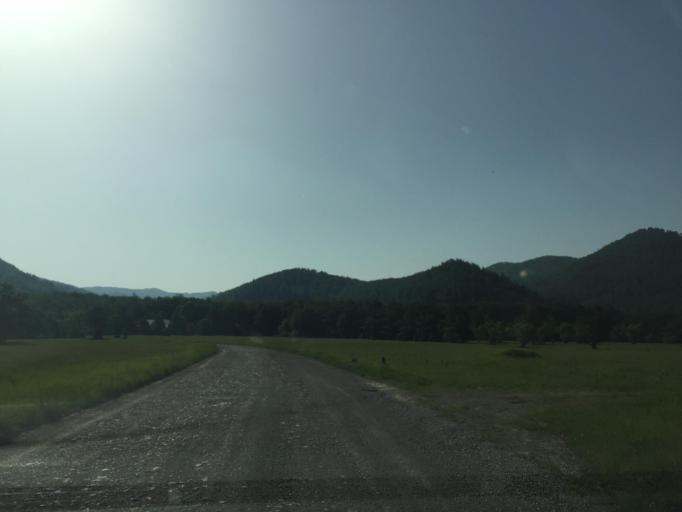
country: HR
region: Primorsko-Goranska
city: Klana
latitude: 45.5047
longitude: 14.4270
